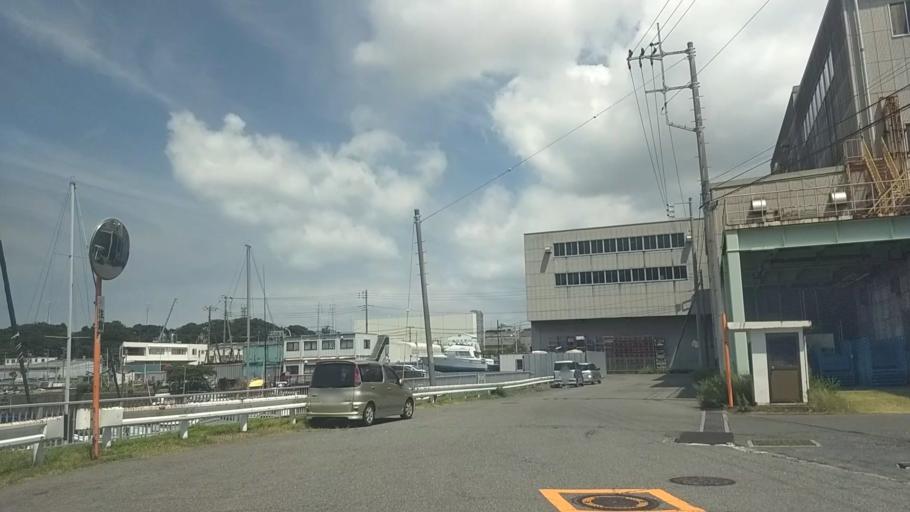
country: JP
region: Kanagawa
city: Yokosuka
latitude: 35.3094
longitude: 139.6399
